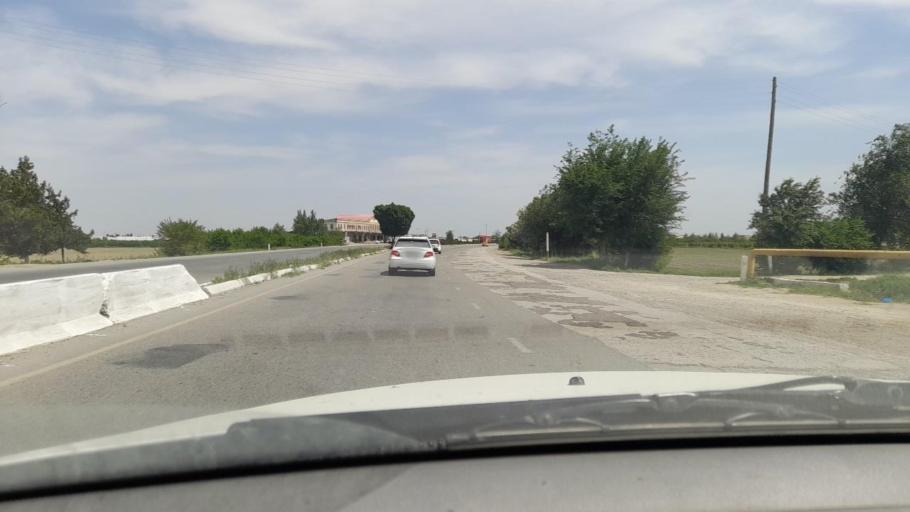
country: UZ
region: Bukhara
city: Wobkent
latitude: 40.0701
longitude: 64.5590
